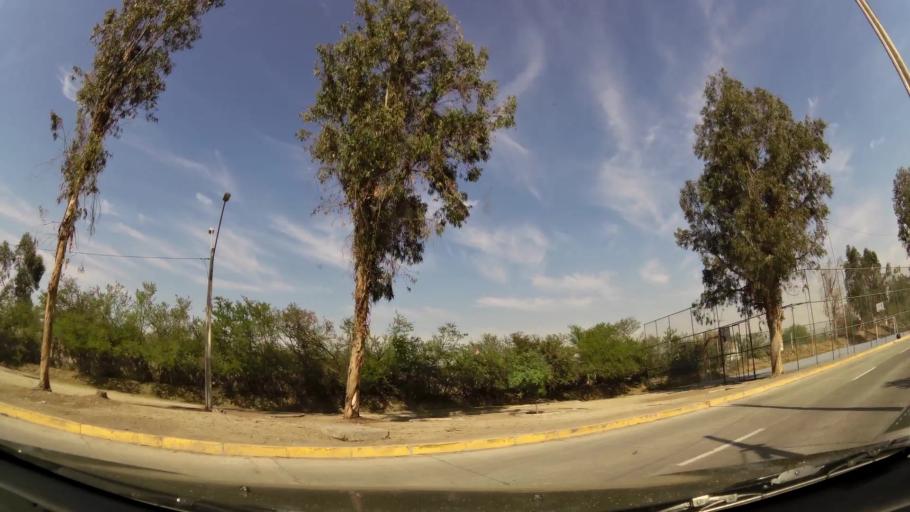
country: CL
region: Santiago Metropolitan
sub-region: Provincia de Cordillera
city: Puente Alto
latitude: -33.5717
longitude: -70.5892
